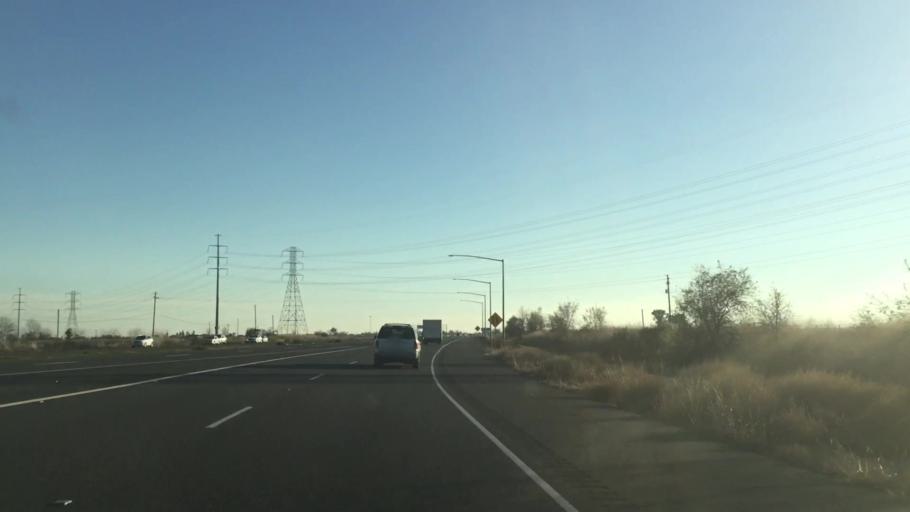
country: US
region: California
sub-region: Sacramento County
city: Elverta
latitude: 38.8449
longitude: -121.5440
